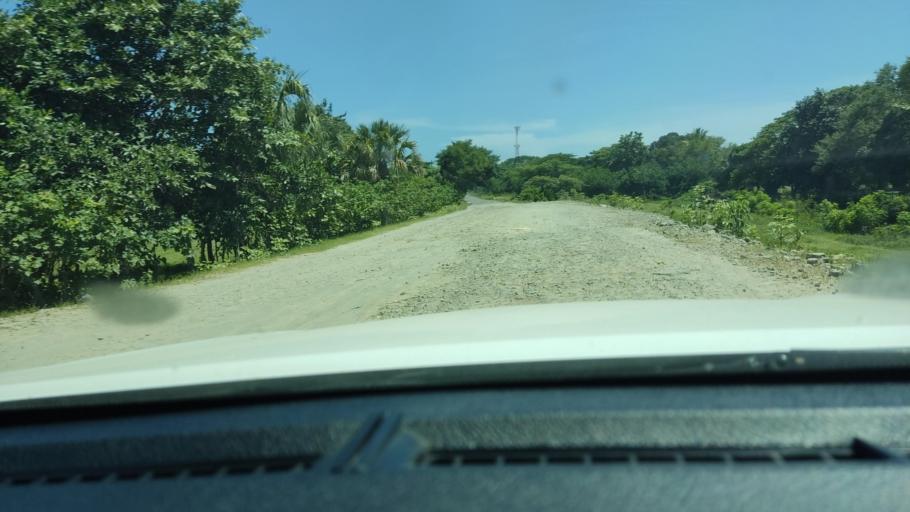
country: SV
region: Ahuachapan
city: San Francisco Menendez
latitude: 13.7575
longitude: -90.1193
